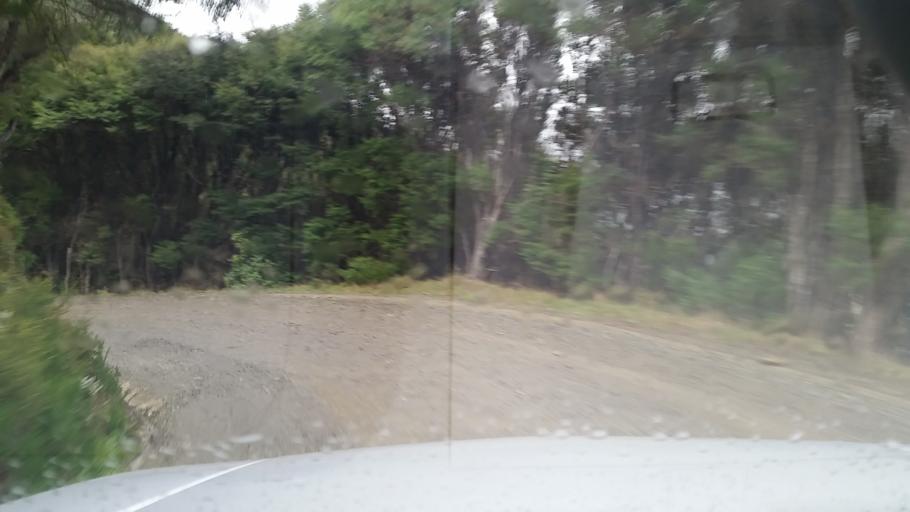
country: NZ
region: Marlborough
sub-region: Marlborough District
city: Picton
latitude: -41.1350
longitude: 174.0535
